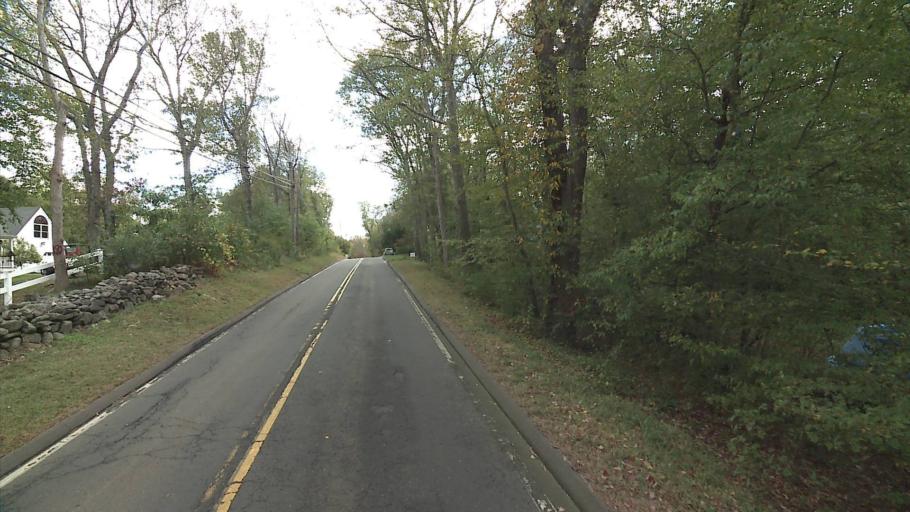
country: US
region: Connecticut
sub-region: Middlesex County
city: Durham
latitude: 41.4143
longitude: -72.6153
